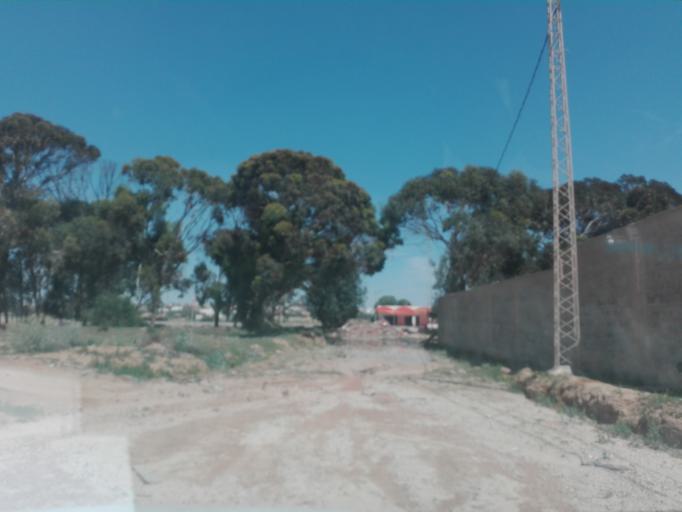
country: TN
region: Safaqis
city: Sfax
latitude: 34.7297
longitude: 10.5193
